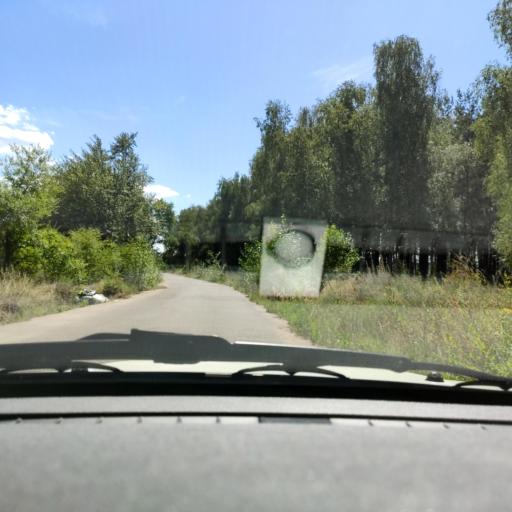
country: RU
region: Voronezj
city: Somovo
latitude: 51.7337
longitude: 39.3200
